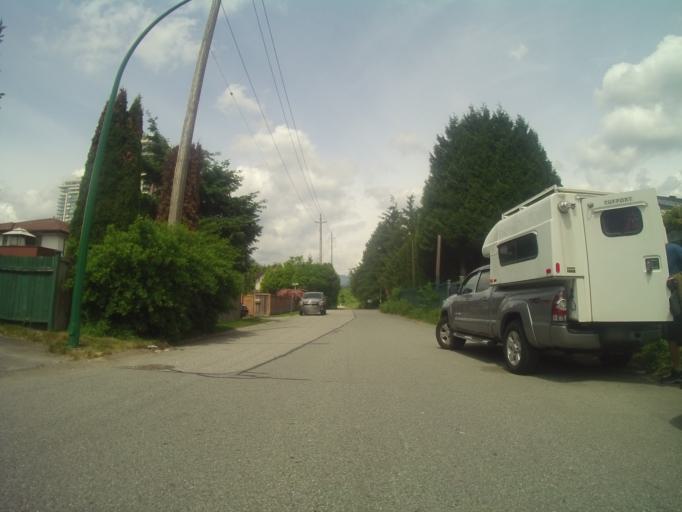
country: CA
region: British Columbia
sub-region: Fraser Valley Regional District
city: North Vancouver
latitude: 49.3101
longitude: -123.0295
